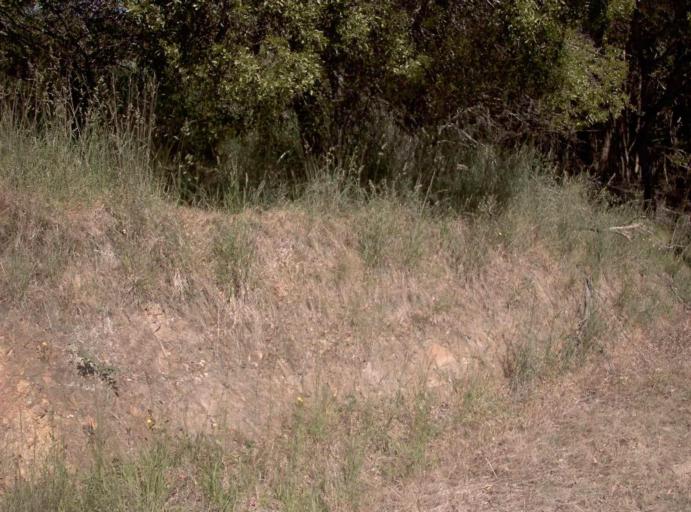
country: AU
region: New South Wales
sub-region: Bombala
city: Bombala
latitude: -37.1673
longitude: 148.7196
